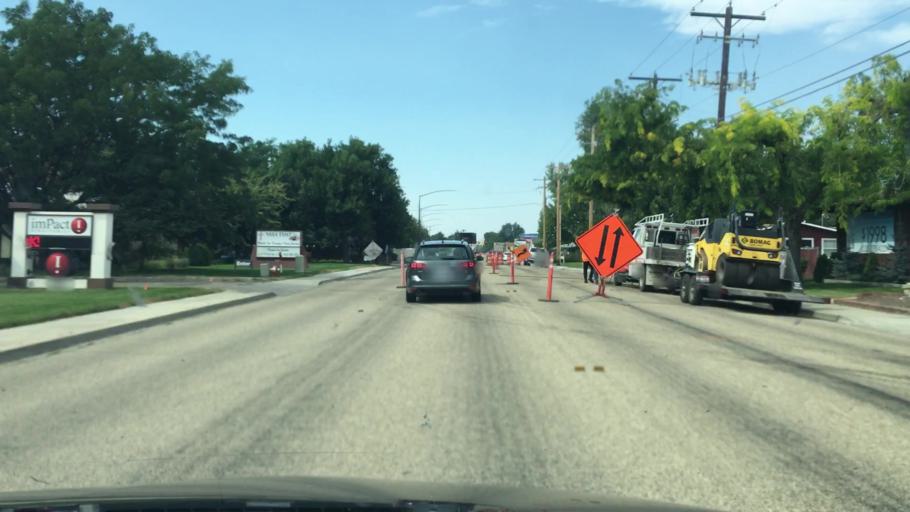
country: US
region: Idaho
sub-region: Ada County
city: Garden City
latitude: 43.6156
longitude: -116.2742
